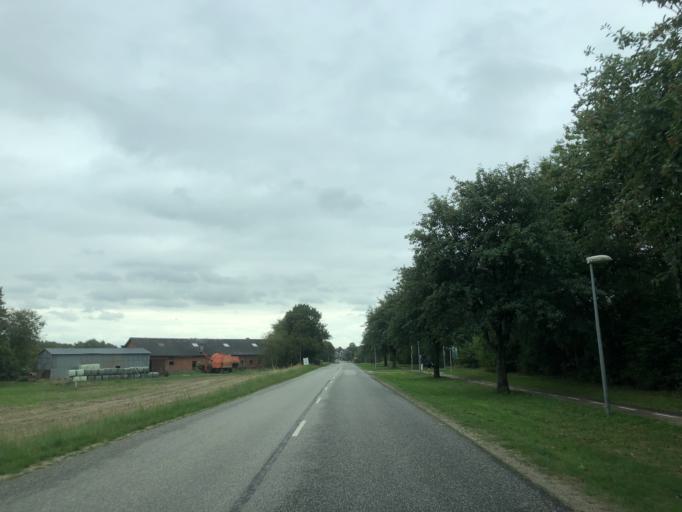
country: DK
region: Central Jutland
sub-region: Herning Kommune
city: Snejbjerg
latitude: 56.1750
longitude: 8.8412
